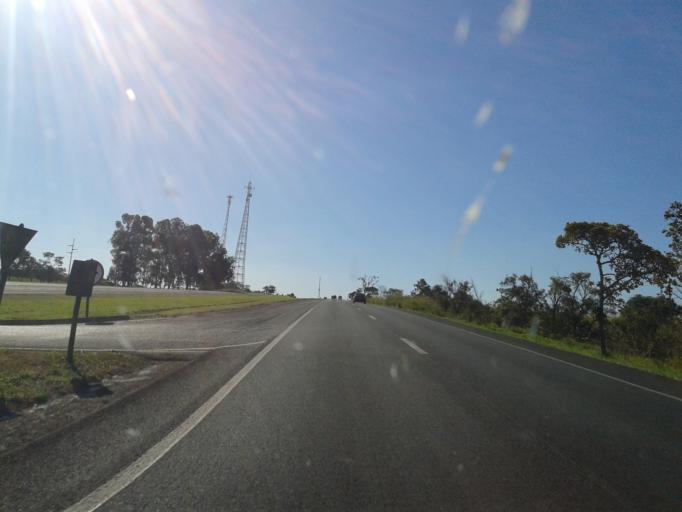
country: BR
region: Minas Gerais
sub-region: Uberlandia
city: Uberlandia
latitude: -19.1415
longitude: -48.1691
